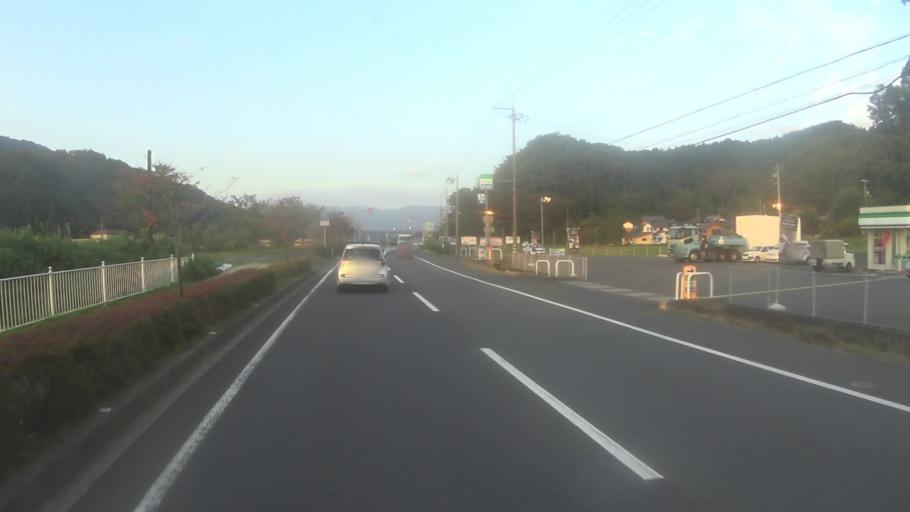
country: JP
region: Kyoto
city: Miyazu
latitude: 35.5441
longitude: 135.1335
